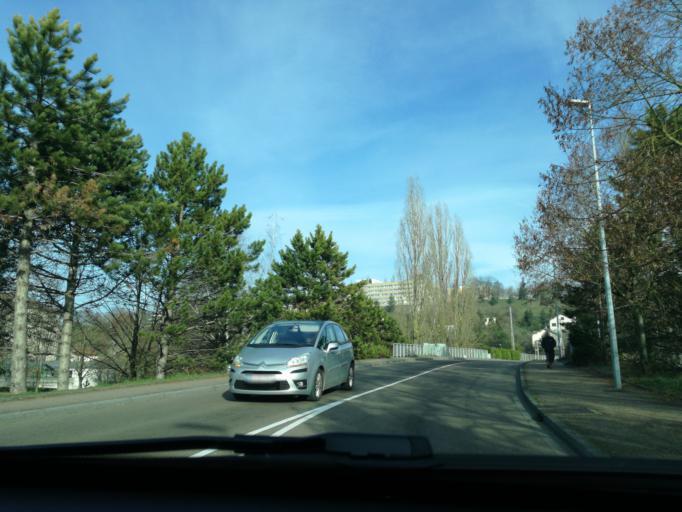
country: FR
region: Lorraine
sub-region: Departement de la Meuse
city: Bar-le-Duc
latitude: 48.7760
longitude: 5.1633
